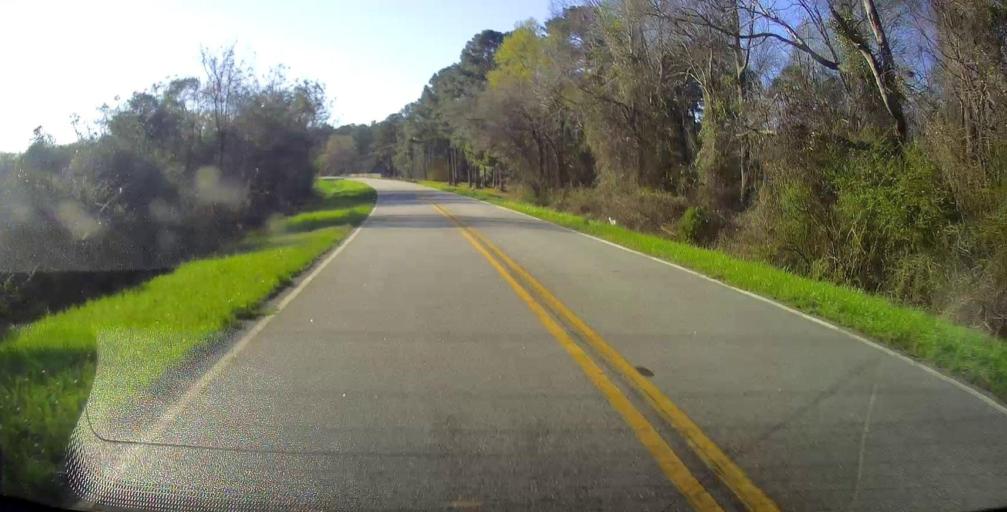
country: US
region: Georgia
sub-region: Houston County
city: Perry
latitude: 32.3597
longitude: -83.6445
